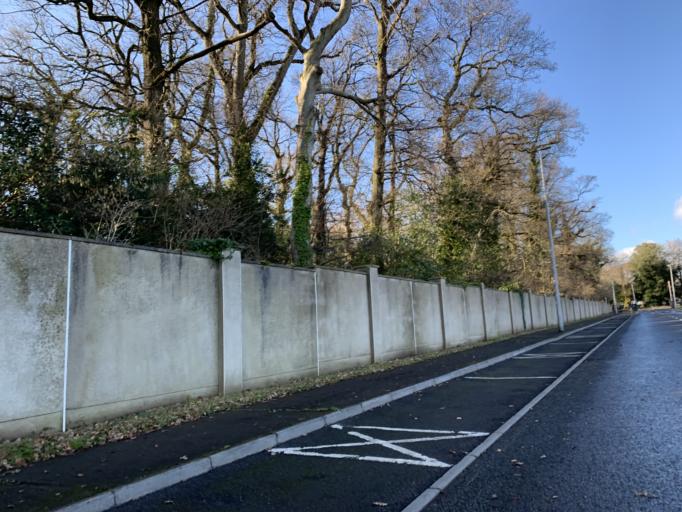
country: IE
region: Leinster
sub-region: Kildare
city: Celbridge
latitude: 53.3332
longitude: -6.5619
